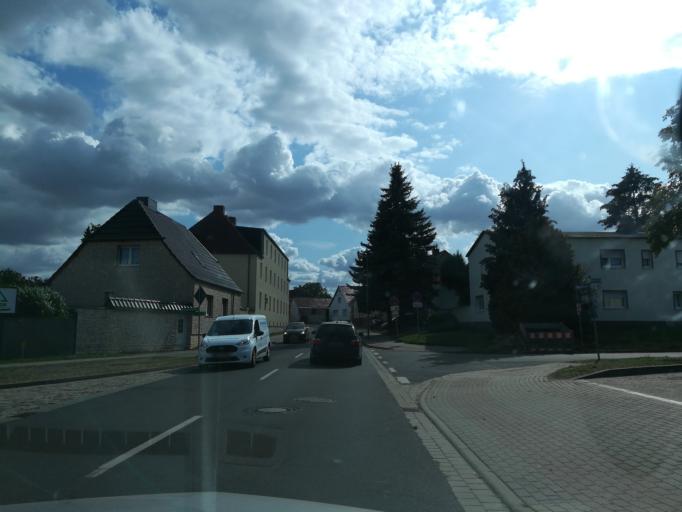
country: DE
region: Saxony-Anhalt
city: Niederndodeleben
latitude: 52.1431
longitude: 11.4956
